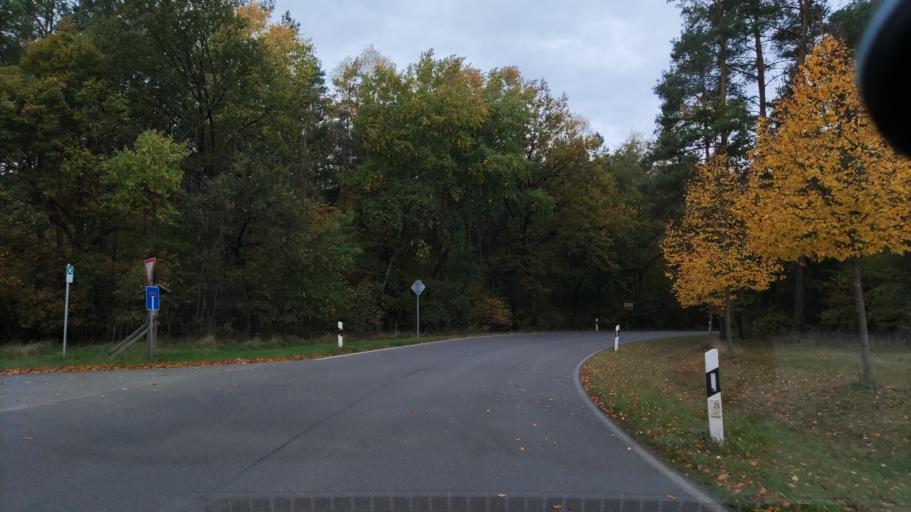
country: DE
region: Mecklenburg-Vorpommern
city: Boizenburg
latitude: 53.3781
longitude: 10.8540
